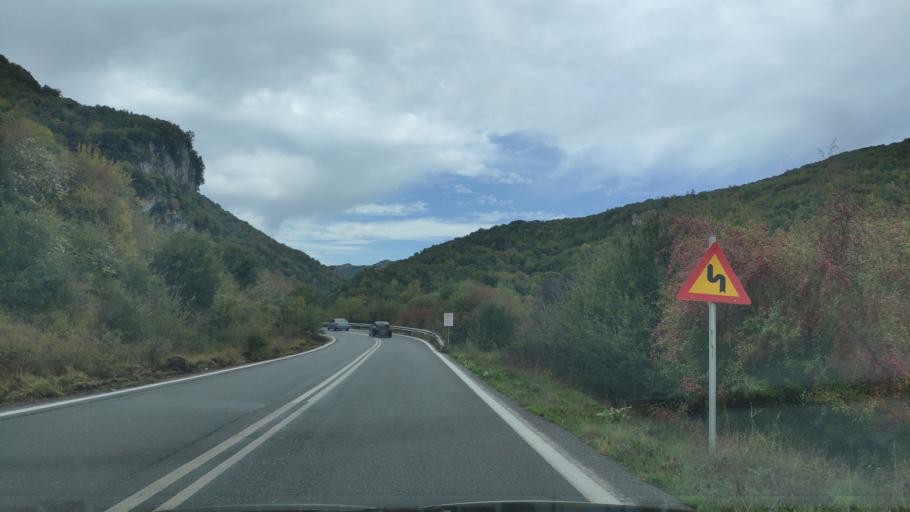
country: GR
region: Peloponnese
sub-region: Nomos Arkadias
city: Dimitsana
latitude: 37.6276
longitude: 22.0630
